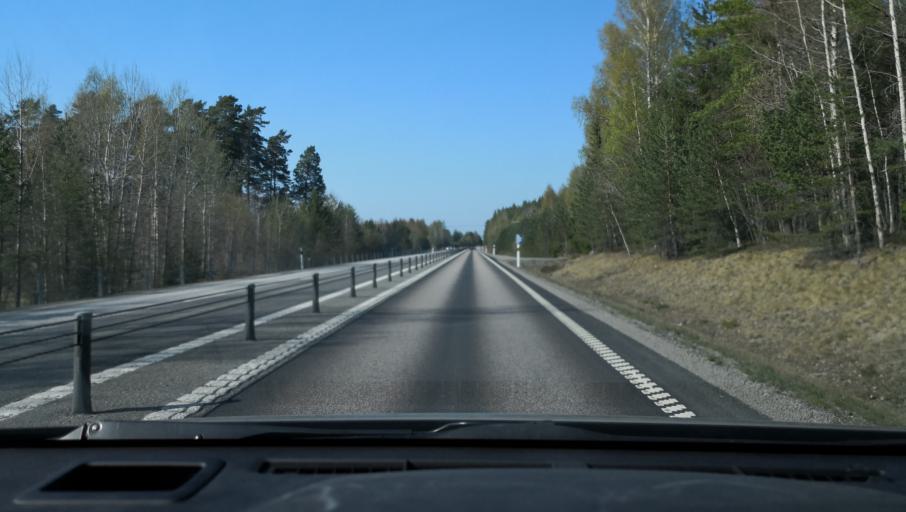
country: SE
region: Uppsala
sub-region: Heby Kommun
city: Tarnsjo
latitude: 60.2128
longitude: 16.9535
